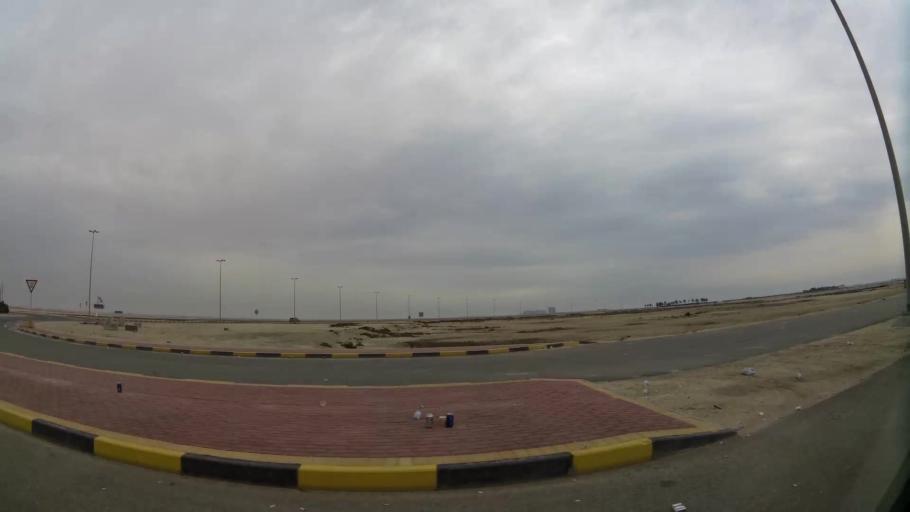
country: BH
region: Central Governorate
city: Dar Kulayb
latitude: 25.8453
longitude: 50.5860
